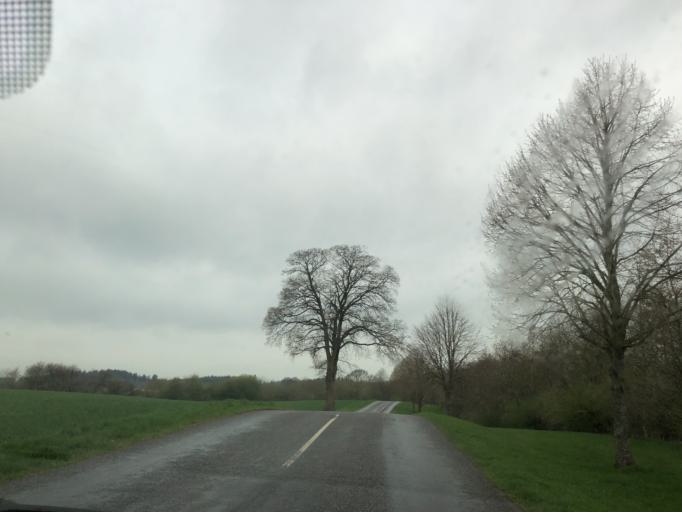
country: DK
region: Zealand
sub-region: Lejre Kommune
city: Kirke Hvalso
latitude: 55.5292
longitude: 11.8542
